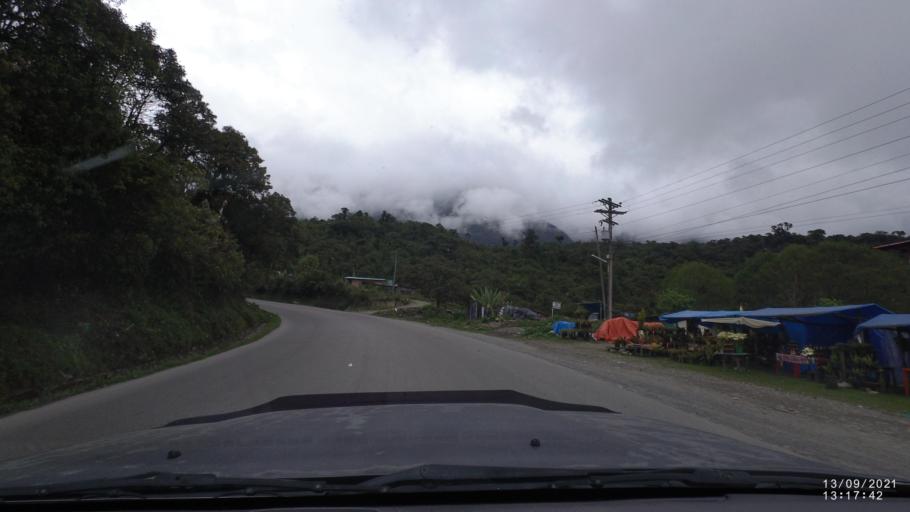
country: BO
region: Cochabamba
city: Colomi
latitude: -17.1978
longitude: -65.8643
